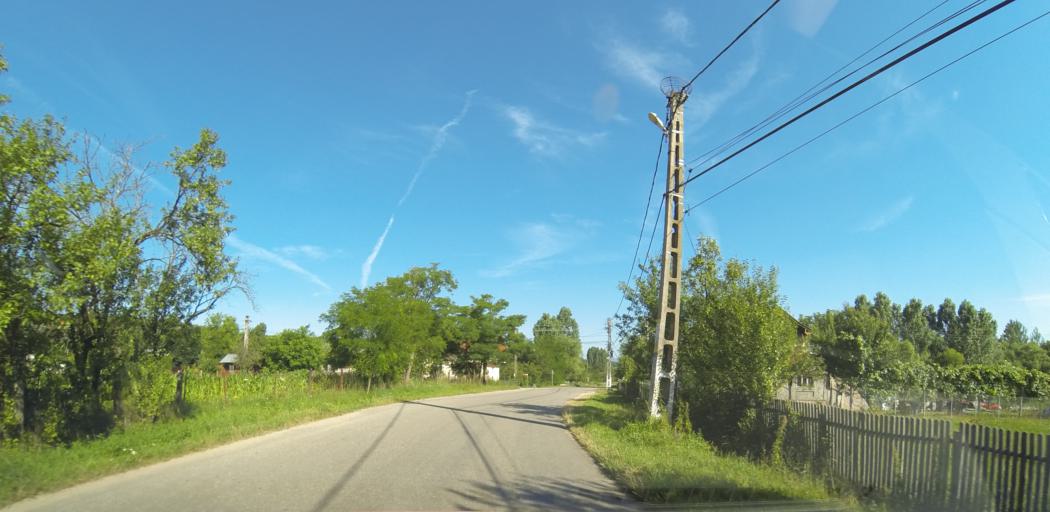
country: RO
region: Valcea
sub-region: Comuna Slatioara
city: Slatioara
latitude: 45.1347
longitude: 23.8751
